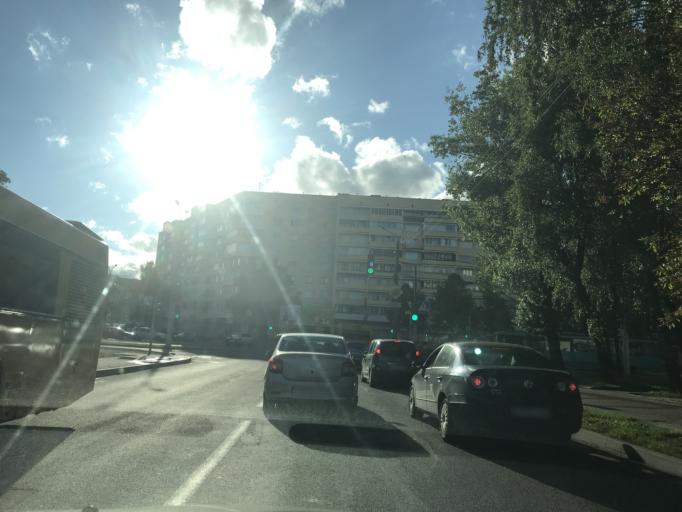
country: BY
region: Minsk
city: Minsk
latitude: 53.9498
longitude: 27.6172
